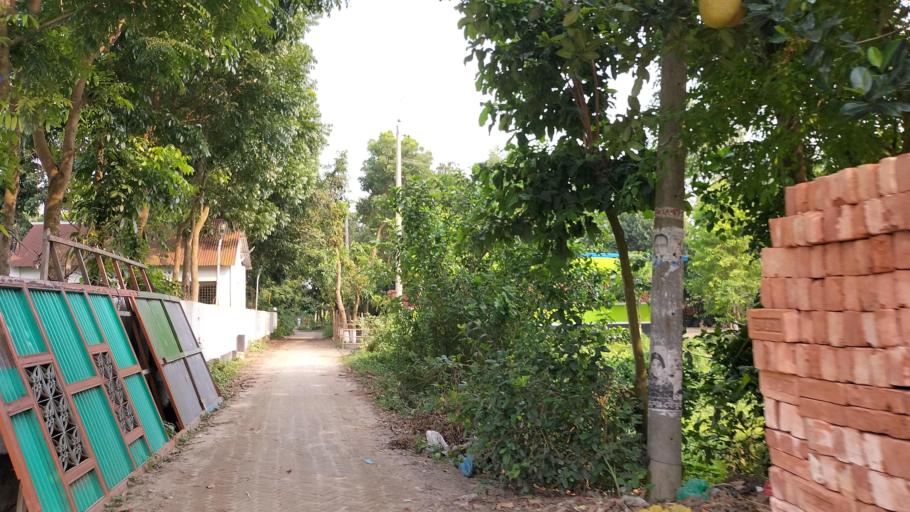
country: BD
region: Dhaka
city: Azimpur
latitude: 23.6707
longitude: 90.3139
